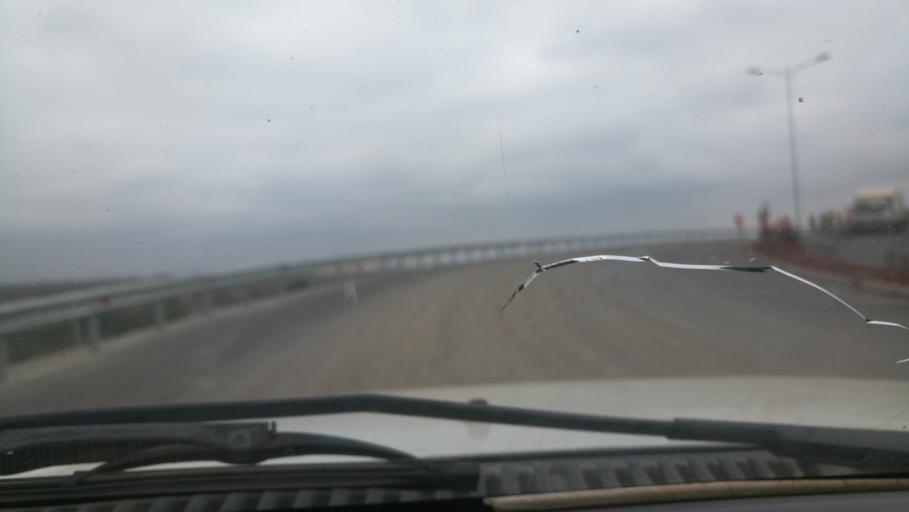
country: KE
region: Nairobi Area
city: Pumwani
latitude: -1.3414
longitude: 36.8869
